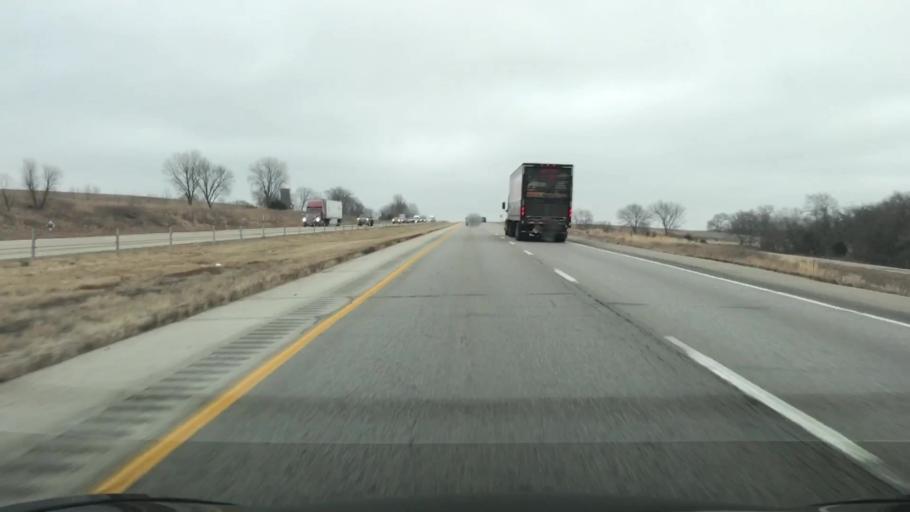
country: US
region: Iowa
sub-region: Madison County
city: Earlham
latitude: 41.5176
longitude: -94.1224
